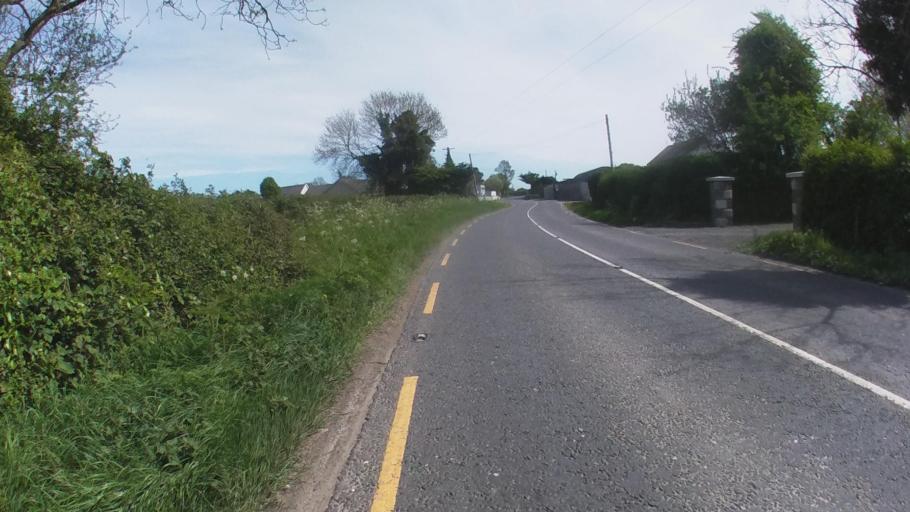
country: IE
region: Leinster
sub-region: County Carlow
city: Carlow
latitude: 52.8446
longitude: -6.9816
